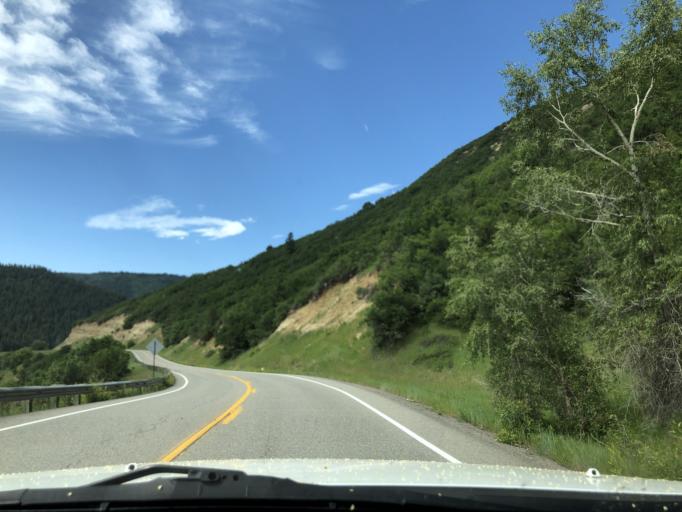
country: US
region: Colorado
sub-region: Delta County
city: Paonia
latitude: 38.9542
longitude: -107.3437
